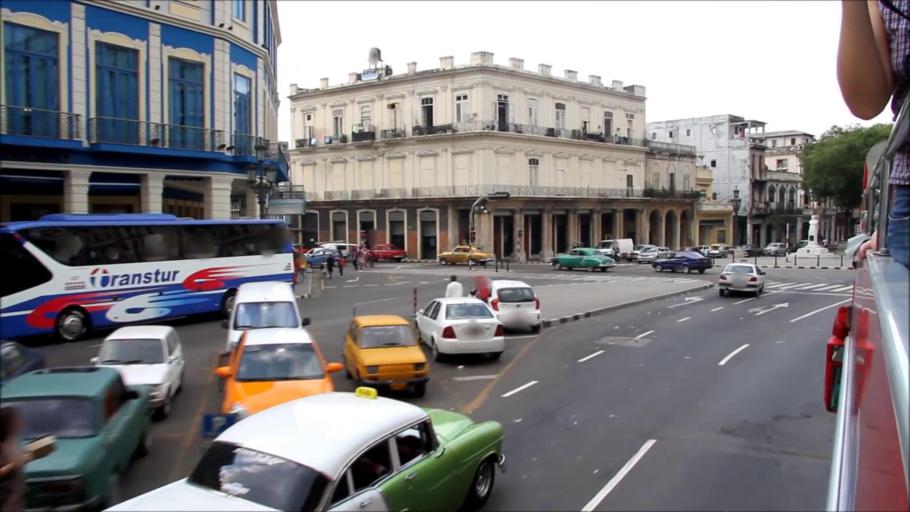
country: CU
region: La Habana
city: Centro Habana
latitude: 23.1380
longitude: -82.3592
